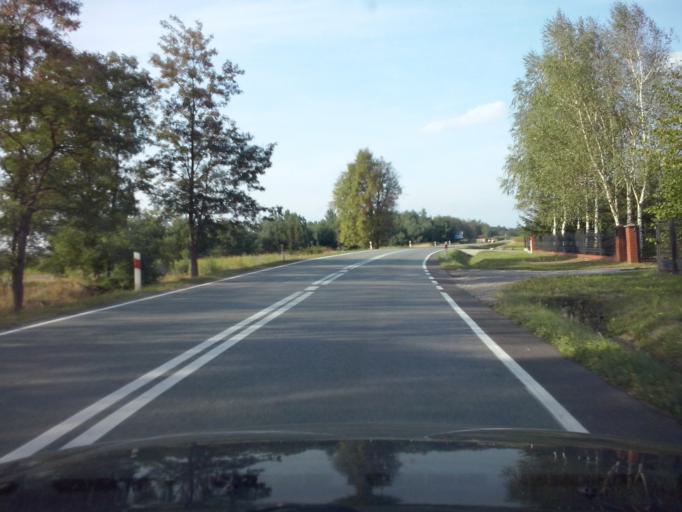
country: PL
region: Subcarpathian Voivodeship
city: Nowa Sarzyna
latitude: 50.3559
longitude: 22.3201
